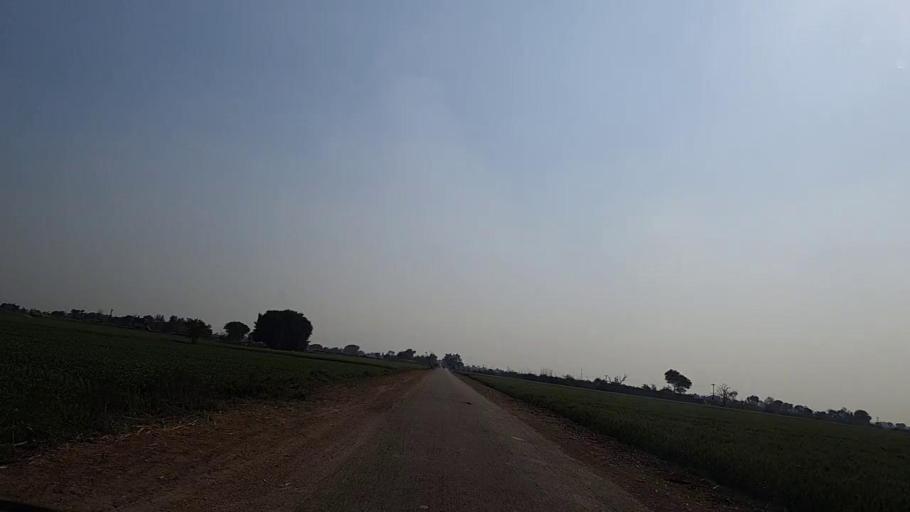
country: PK
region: Sindh
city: Sakrand
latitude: 26.0847
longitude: 68.2901
